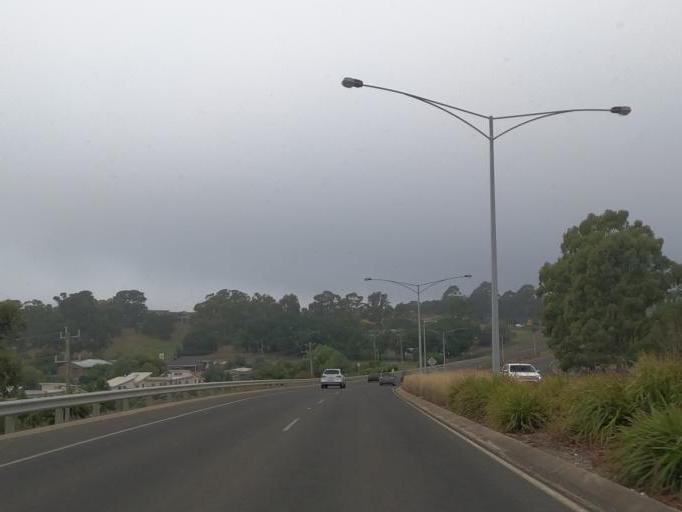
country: AU
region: Victoria
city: Brown Hill
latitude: -37.5592
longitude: 143.9021
